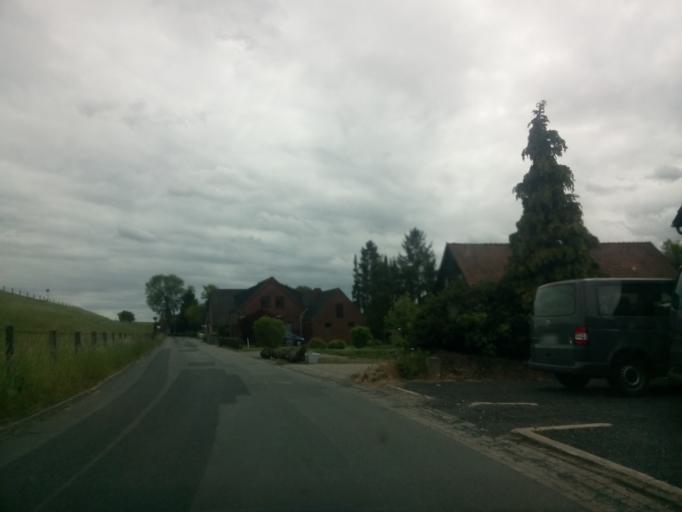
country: DE
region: Lower Saxony
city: Lemwerder
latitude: 53.1718
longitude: 8.5736
